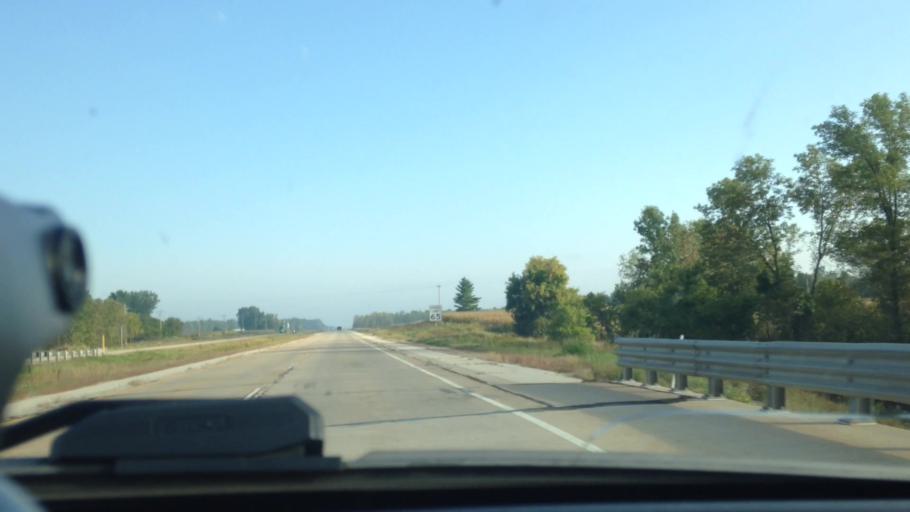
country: US
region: Wisconsin
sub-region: Oconto County
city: Oconto Falls
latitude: 45.0099
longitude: -88.0447
